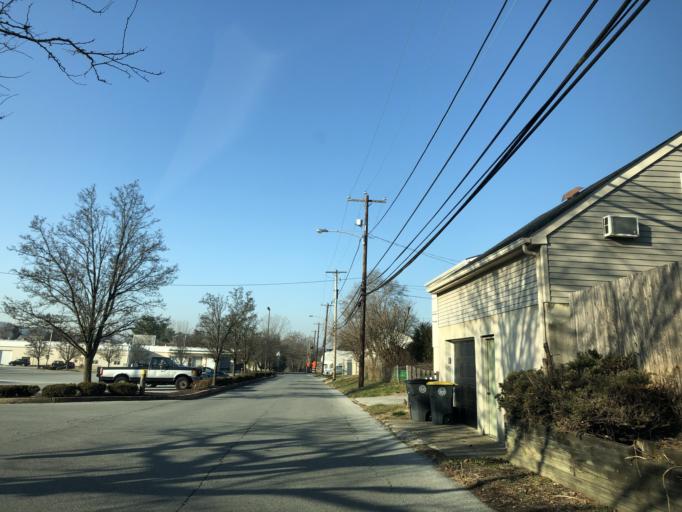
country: US
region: Pennsylvania
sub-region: Chester County
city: Downingtown
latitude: 40.0063
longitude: -75.6921
